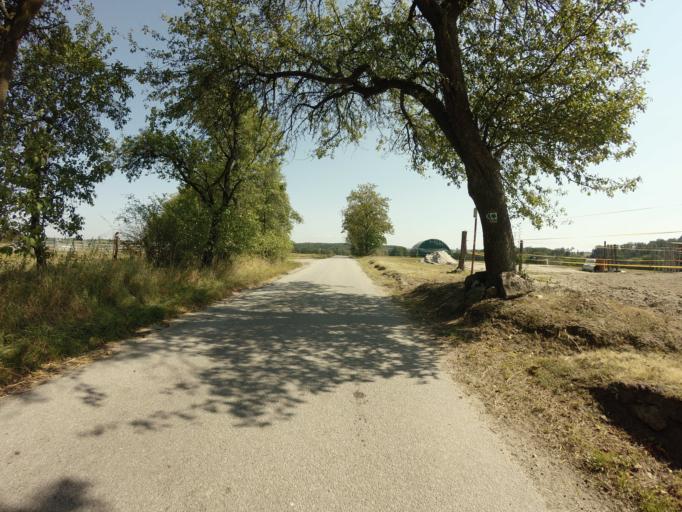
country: CZ
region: Jihocesky
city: Kamenny Ujezd
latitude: 48.8862
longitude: 14.4067
